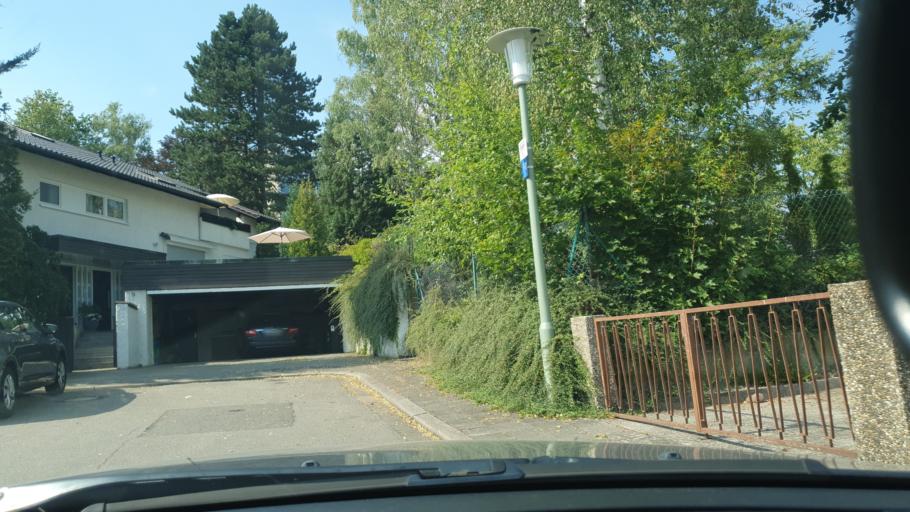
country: DE
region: Rheinland-Pfalz
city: Stelzenberg
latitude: 49.4288
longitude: 7.7264
